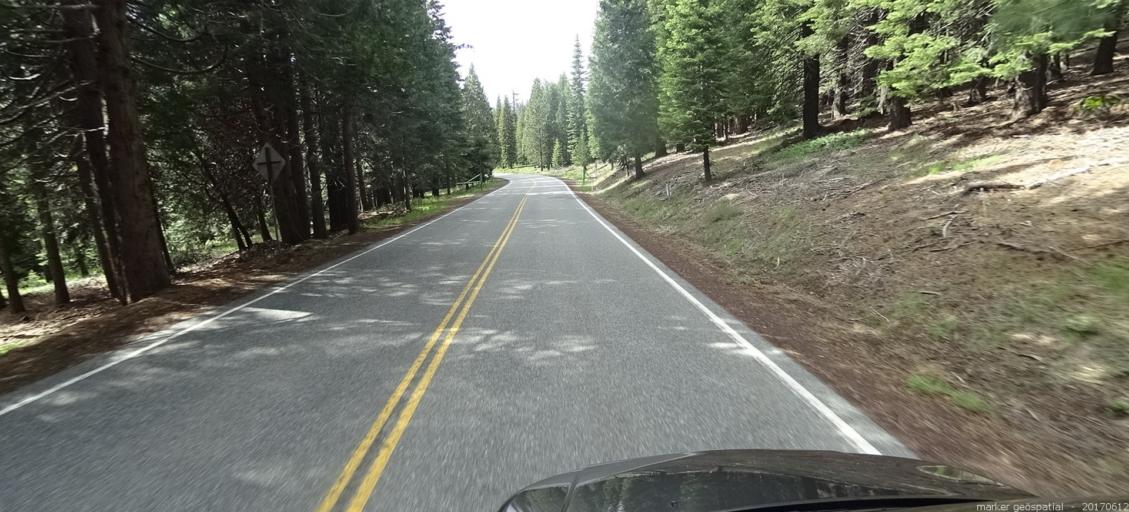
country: US
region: California
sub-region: Siskiyou County
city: Mount Shasta
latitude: 41.3472
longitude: -122.2773
